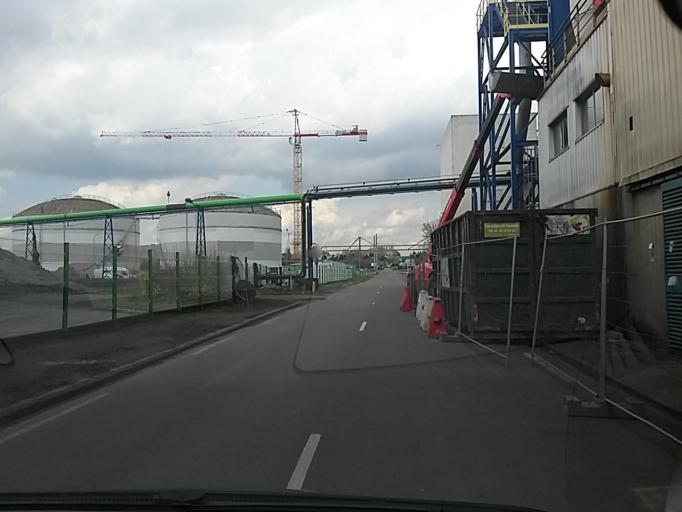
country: FR
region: Picardie
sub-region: Departement de l'Oise
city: Grandfresnoy
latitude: 49.3603
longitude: 2.6663
